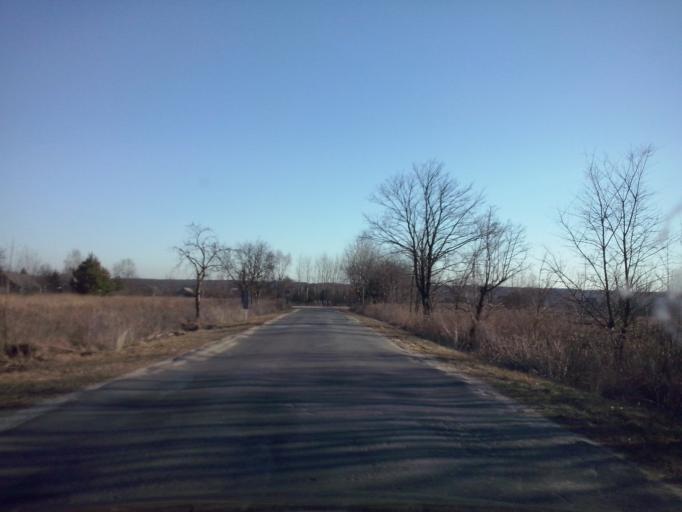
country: PL
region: Subcarpathian Voivodeship
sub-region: Powiat nizanski
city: Harasiuki
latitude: 50.5294
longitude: 22.4464
